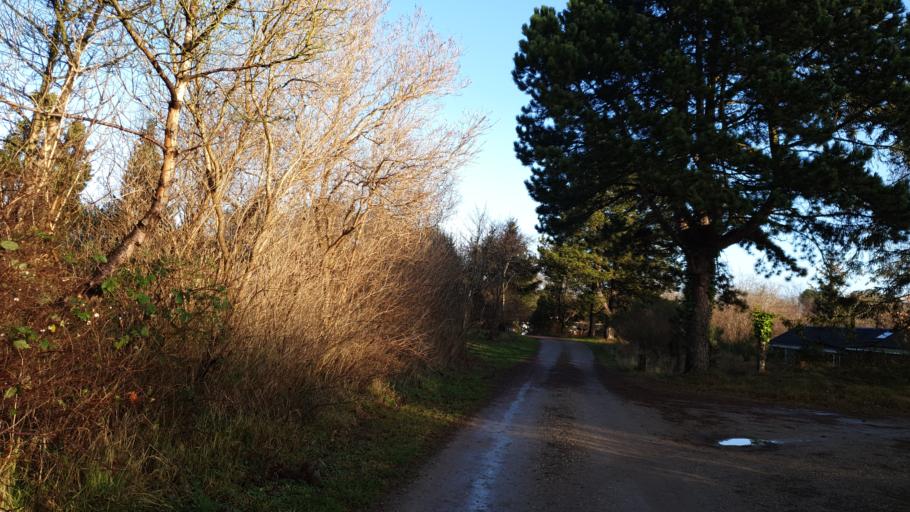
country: DK
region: Zealand
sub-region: Odsherred Kommune
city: Hojby
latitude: 55.9348
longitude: 11.6176
